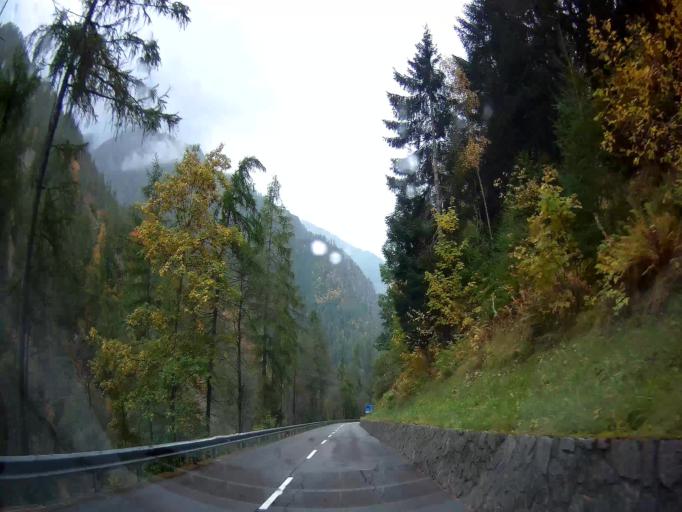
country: IT
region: Trentino-Alto Adige
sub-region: Bolzano
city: Senales
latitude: 46.7072
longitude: 10.9104
